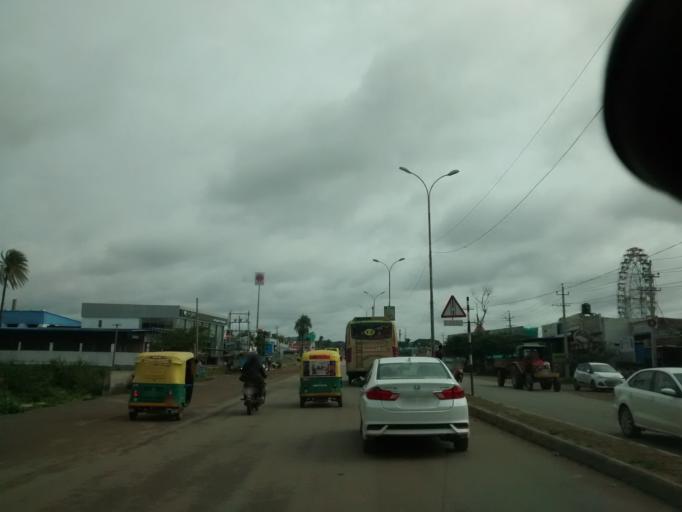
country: IN
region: Karnataka
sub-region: Tumkur
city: Tumkur
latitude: 13.3535
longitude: 77.1033
